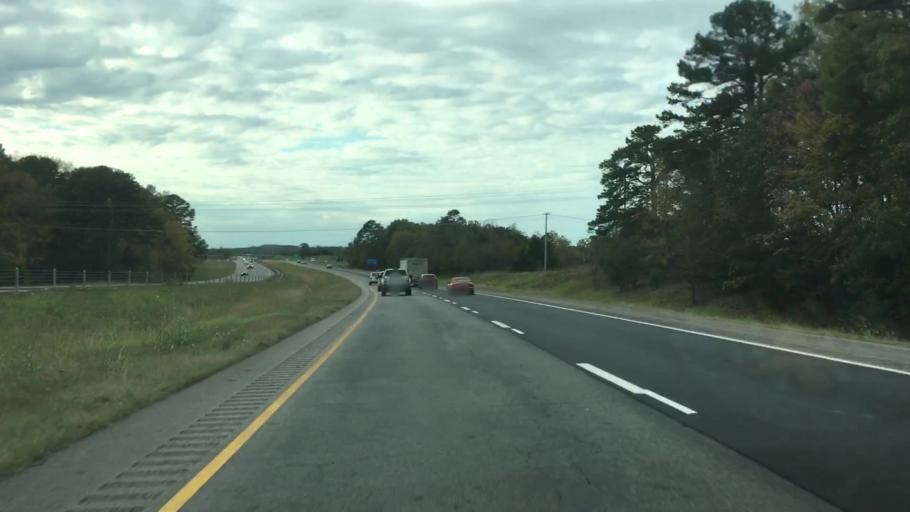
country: US
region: Arkansas
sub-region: Conway County
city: Morrilton
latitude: 35.1739
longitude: -92.7042
